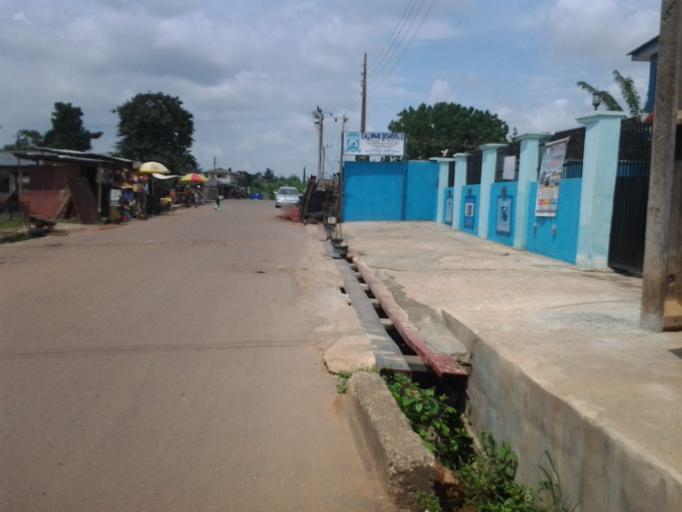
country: NG
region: Oyo
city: Ibadan
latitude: 7.4367
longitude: 3.9518
